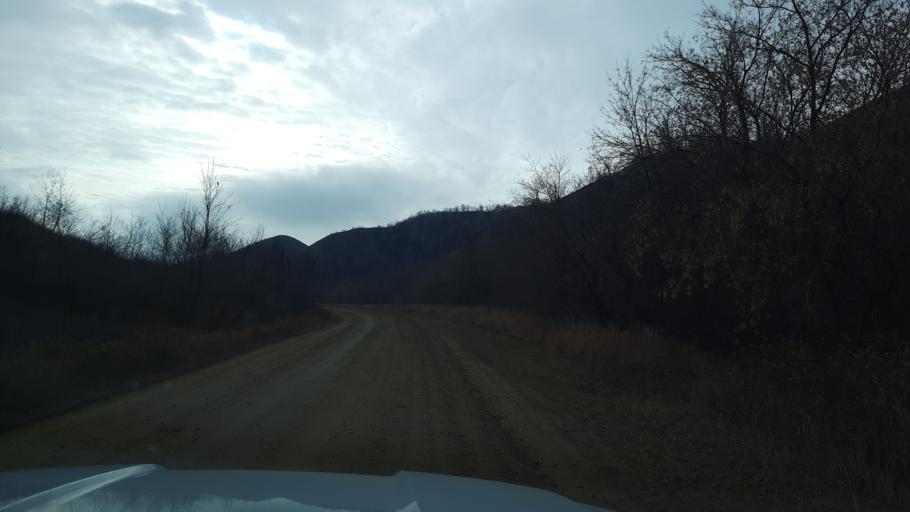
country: CA
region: Saskatchewan
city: White City
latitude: 50.7752
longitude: -104.1346
